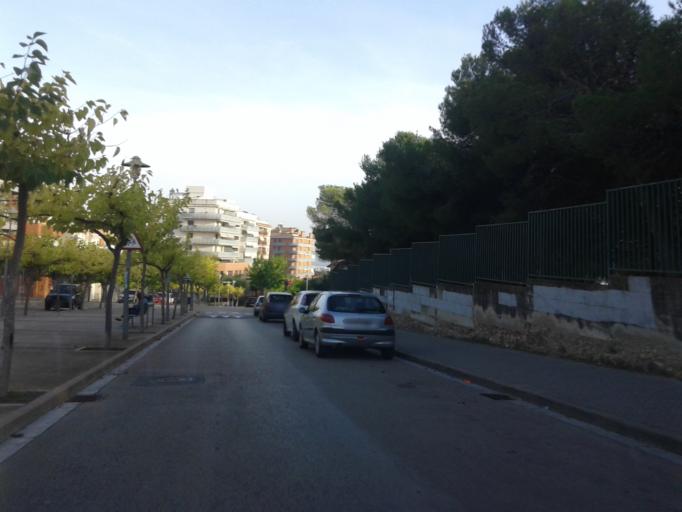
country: ES
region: Catalonia
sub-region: Provincia de Barcelona
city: Vilanova i la Geltru
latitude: 41.2196
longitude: 1.7088
